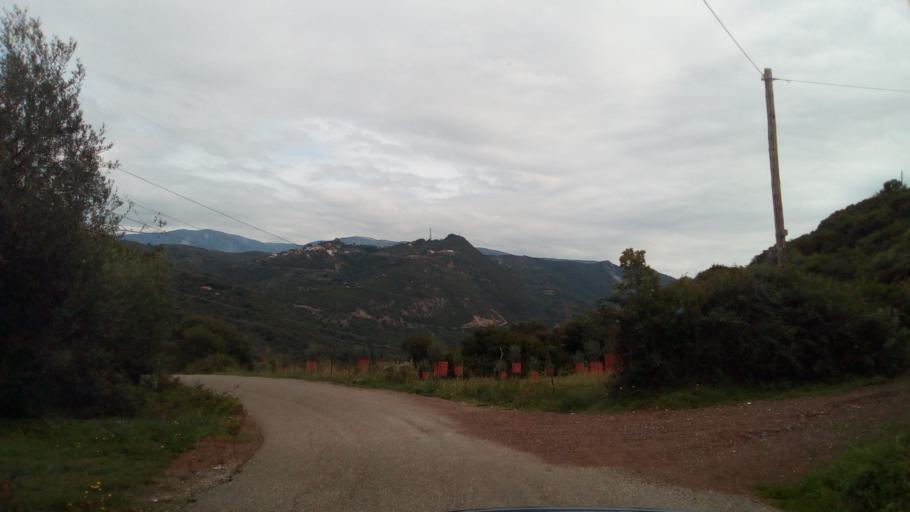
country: GR
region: West Greece
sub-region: Nomos Achaias
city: Kamarai
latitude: 38.4098
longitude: 21.9516
